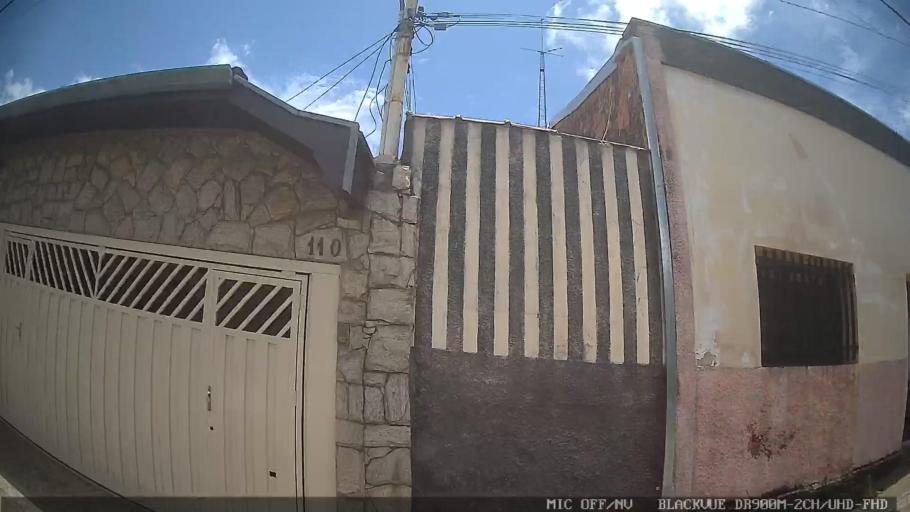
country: BR
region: Sao Paulo
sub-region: Laranjal Paulista
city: Laranjal Paulista
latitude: -23.0484
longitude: -47.8381
